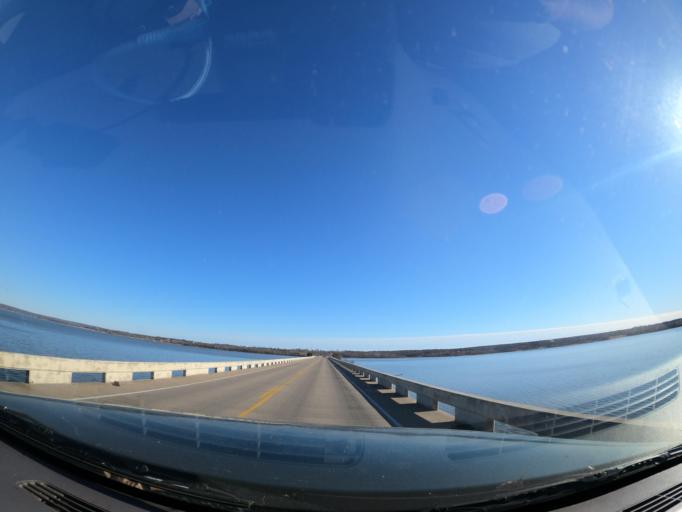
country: US
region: Oklahoma
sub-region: McIntosh County
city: Eufaula
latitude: 35.2459
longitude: -95.5649
